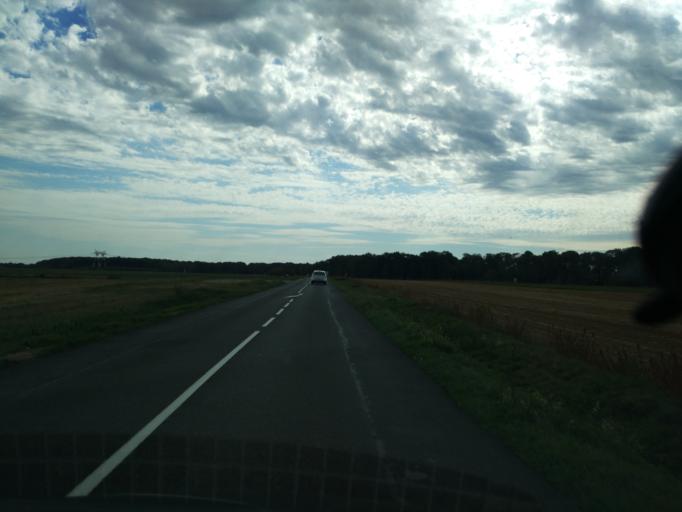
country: FR
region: Ile-de-France
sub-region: Departement de l'Essonne
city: Briis-sous-Forges
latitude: 48.6452
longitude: 2.1207
